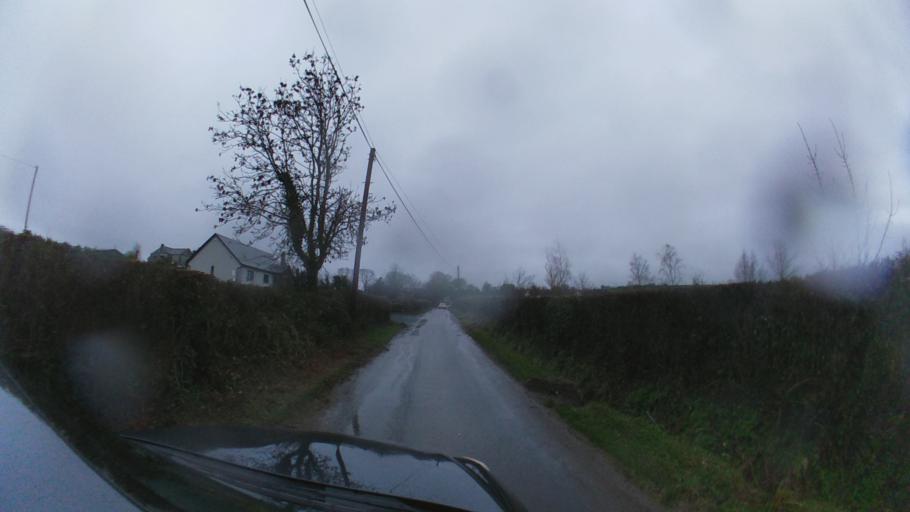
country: IE
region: Leinster
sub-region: Kilkenny
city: Graiguenamanagh
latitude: 52.5933
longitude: -6.9929
